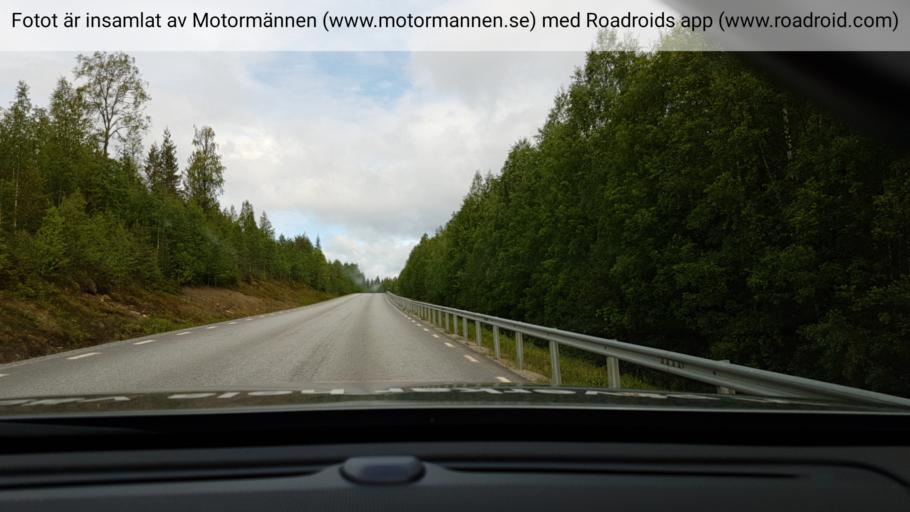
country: SE
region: Vaesterbotten
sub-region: Lycksele Kommun
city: Lycksele
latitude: 64.0327
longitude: 18.6222
